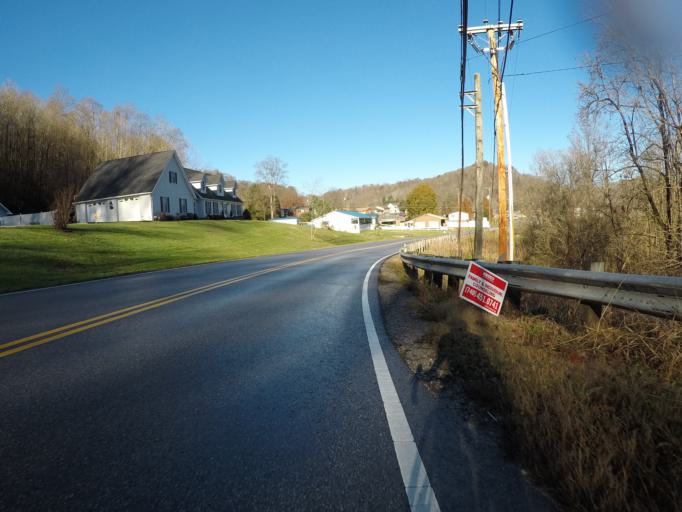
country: US
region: West Virginia
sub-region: Cabell County
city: Huntington
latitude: 38.4320
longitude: -82.4640
